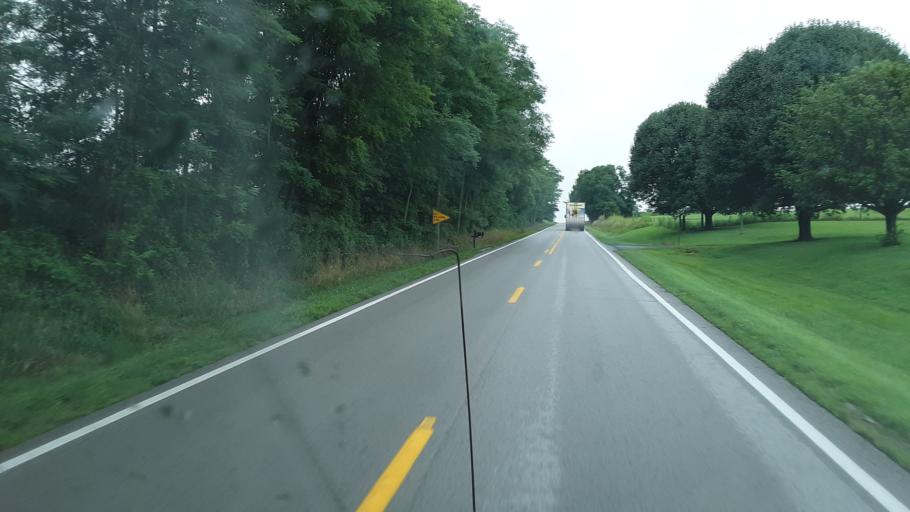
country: US
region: Kentucky
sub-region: Todd County
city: Elkton
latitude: 36.7540
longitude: -87.0388
